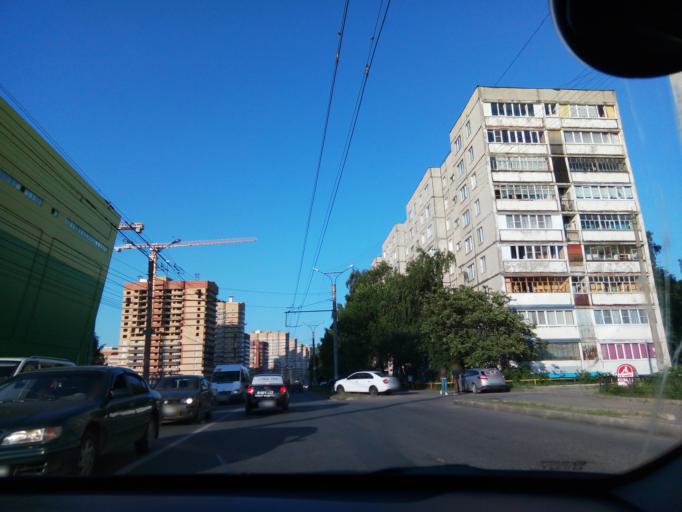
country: RU
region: Chuvashia
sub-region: Cheboksarskiy Rayon
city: Cheboksary
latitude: 56.1067
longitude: 47.2806
